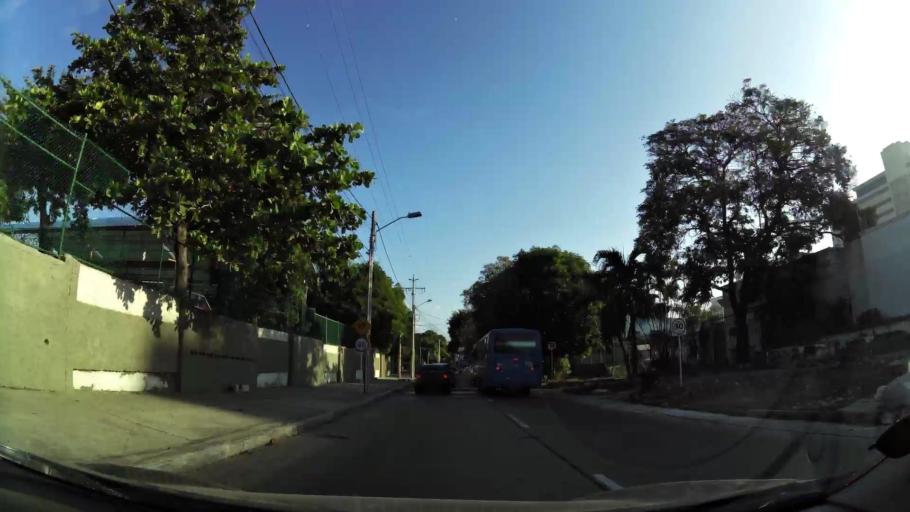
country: CO
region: Atlantico
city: Barranquilla
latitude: 11.0063
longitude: -74.8213
